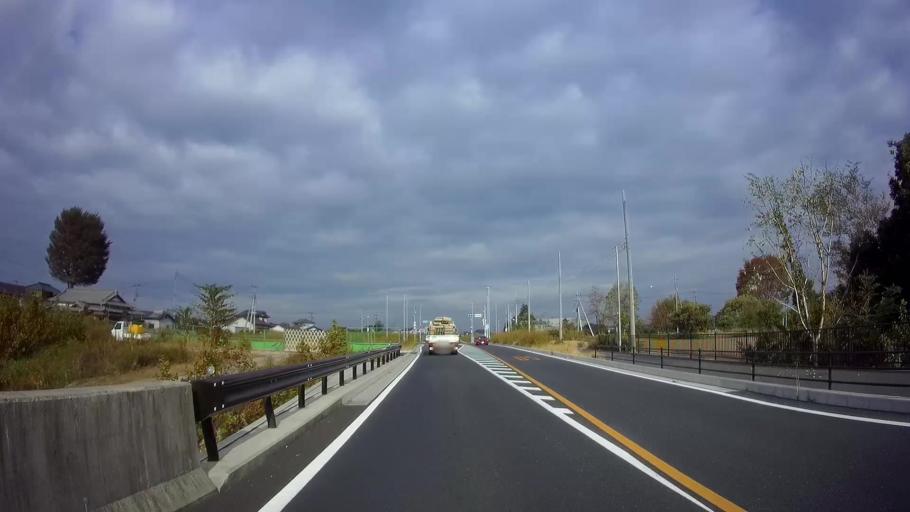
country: JP
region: Saitama
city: Okegawa
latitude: 35.9765
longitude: 139.5397
